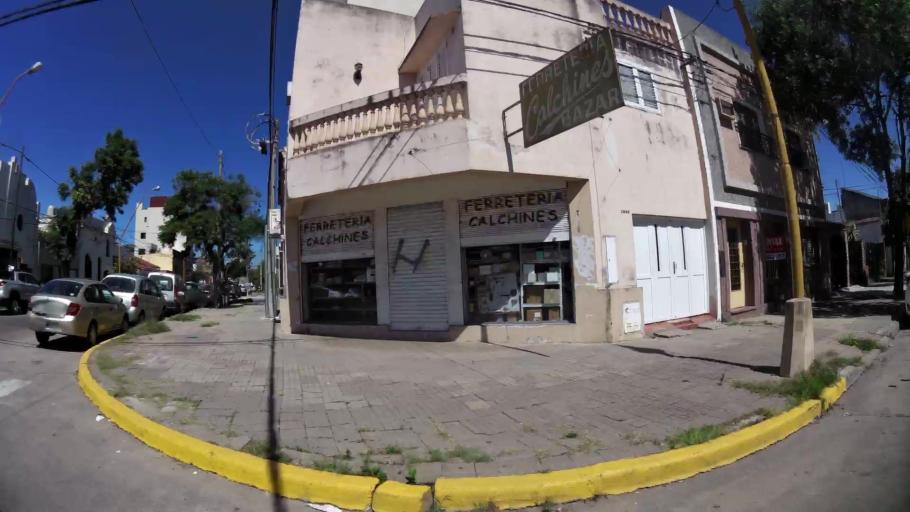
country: AR
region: Santa Fe
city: Santa Fe de la Vera Cruz
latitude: -31.6422
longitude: -60.6958
